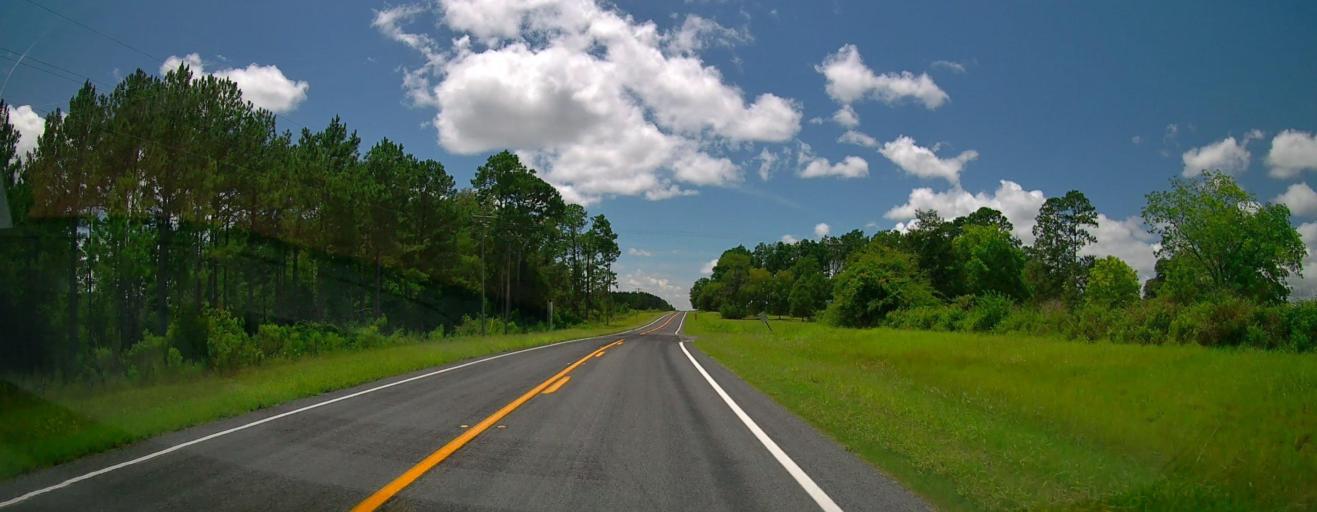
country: US
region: Georgia
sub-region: Turner County
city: Ashburn
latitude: 31.7806
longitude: -83.6069
